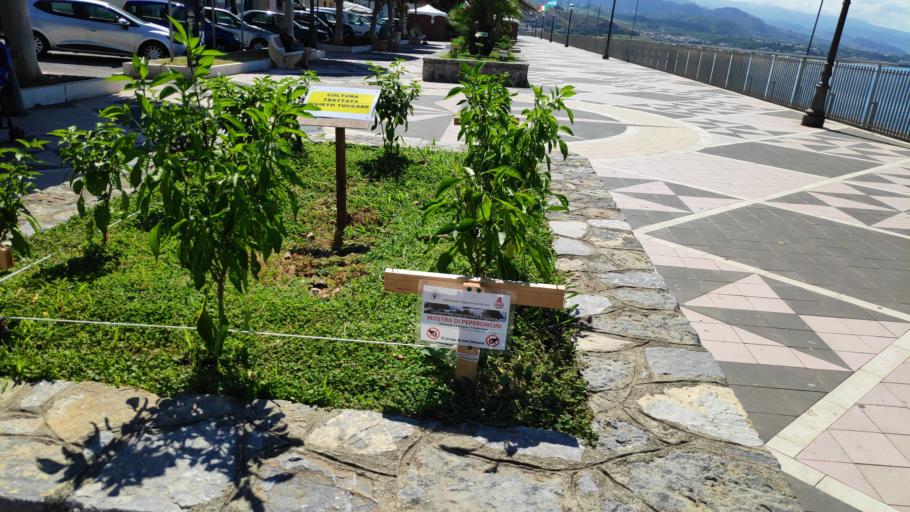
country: IT
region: Calabria
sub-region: Provincia di Cosenza
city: Diamante
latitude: 39.6762
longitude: 15.8200
